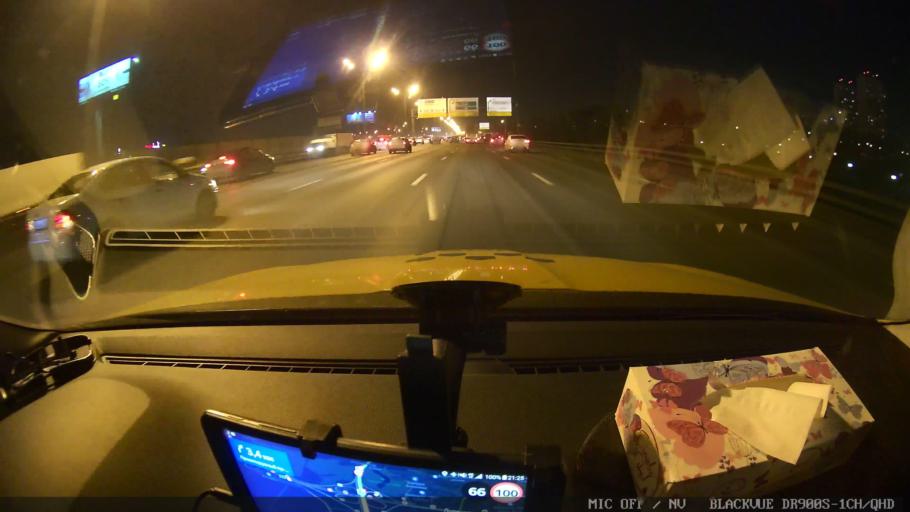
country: RU
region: Moscow
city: Biryulevo
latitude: 55.5787
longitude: 37.6980
